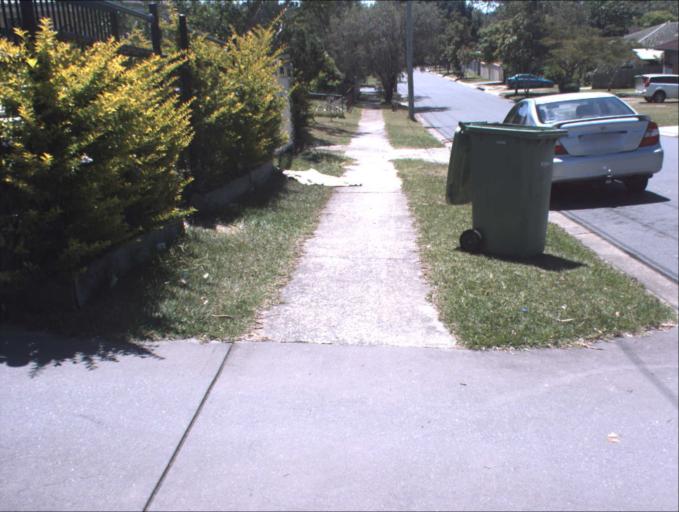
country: AU
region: Queensland
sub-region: Logan
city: Woodridge
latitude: -27.6252
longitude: 153.1076
